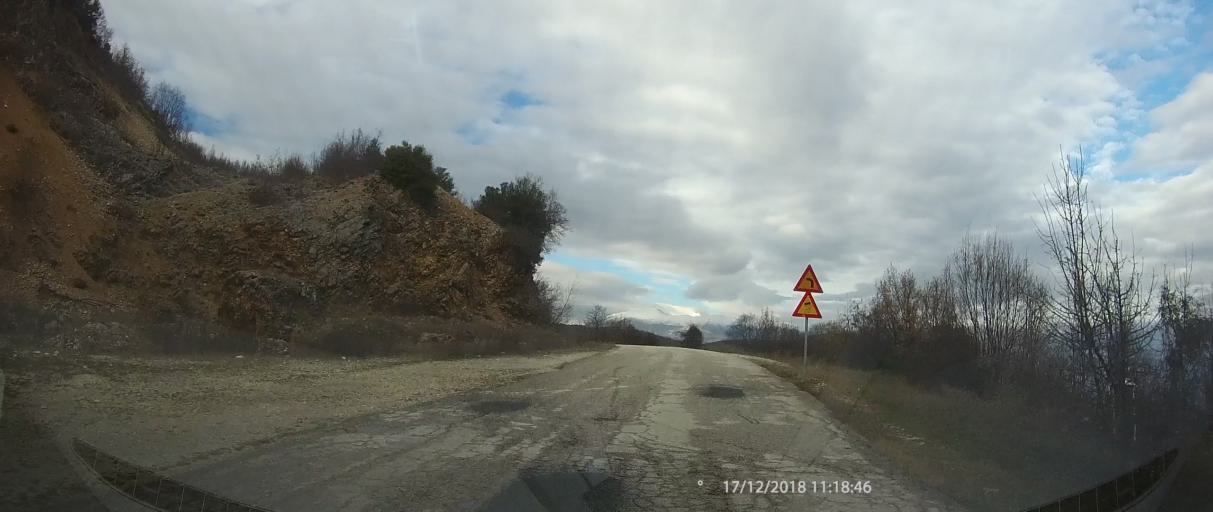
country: GR
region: Epirus
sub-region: Nomos Ioanninon
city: Kalpaki
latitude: 39.9559
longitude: 20.6556
